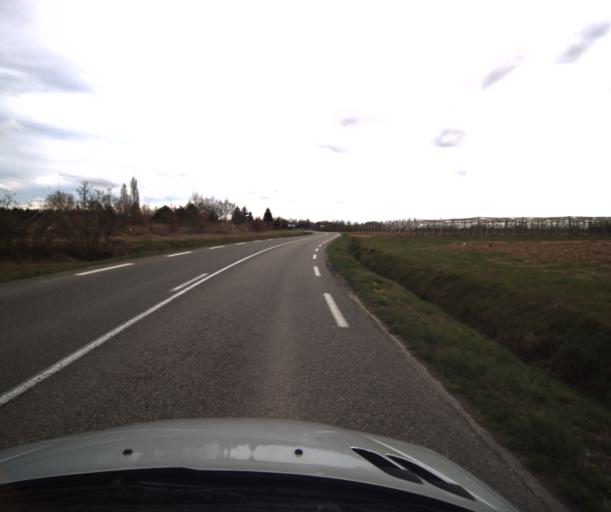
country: FR
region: Midi-Pyrenees
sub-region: Departement du Tarn-et-Garonne
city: Montbeton
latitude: 44.0368
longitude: 1.3105
